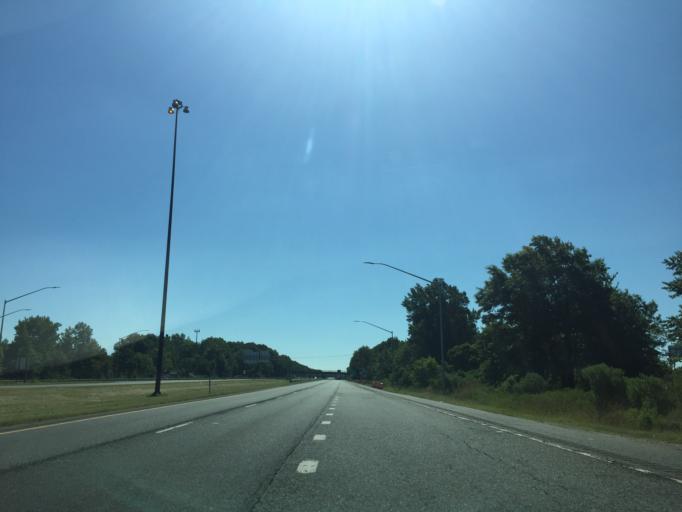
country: US
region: Maryland
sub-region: Baltimore County
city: Essex
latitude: 39.2836
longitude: -76.4902
